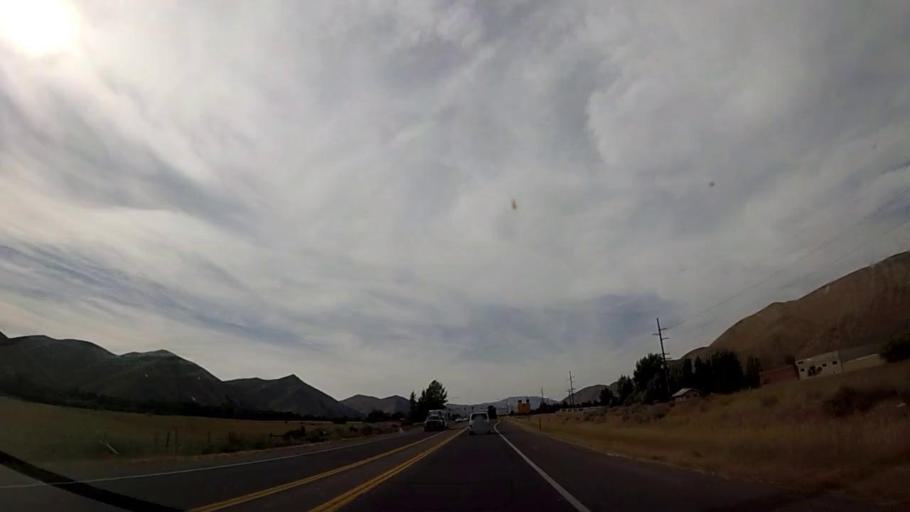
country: US
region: Idaho
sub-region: Blaine County
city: Bellevue
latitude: 43.4845
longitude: -114.2751
